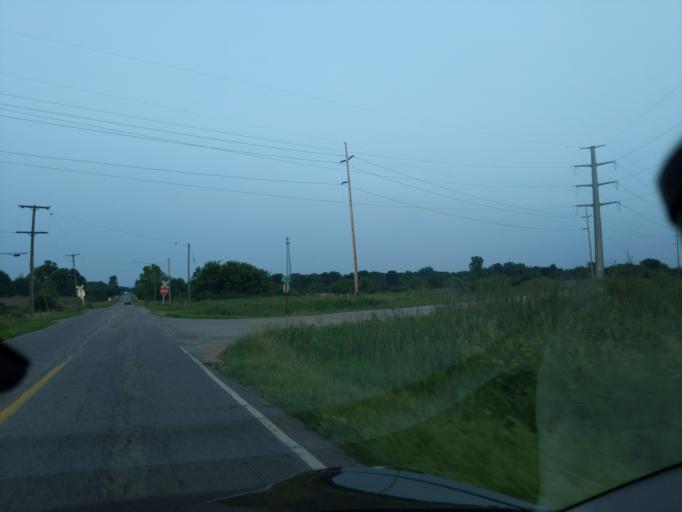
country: US
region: Michigan
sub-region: Jackson County
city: Jackson
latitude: 42.3274
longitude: -84.4398
